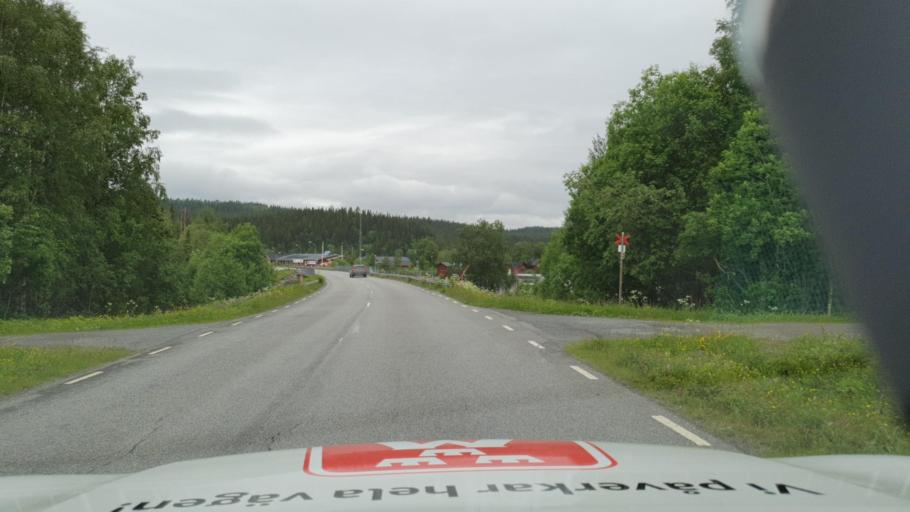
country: SE
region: Jaemtland
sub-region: Are Kommun
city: Are
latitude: 63.7002
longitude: 12.9617
